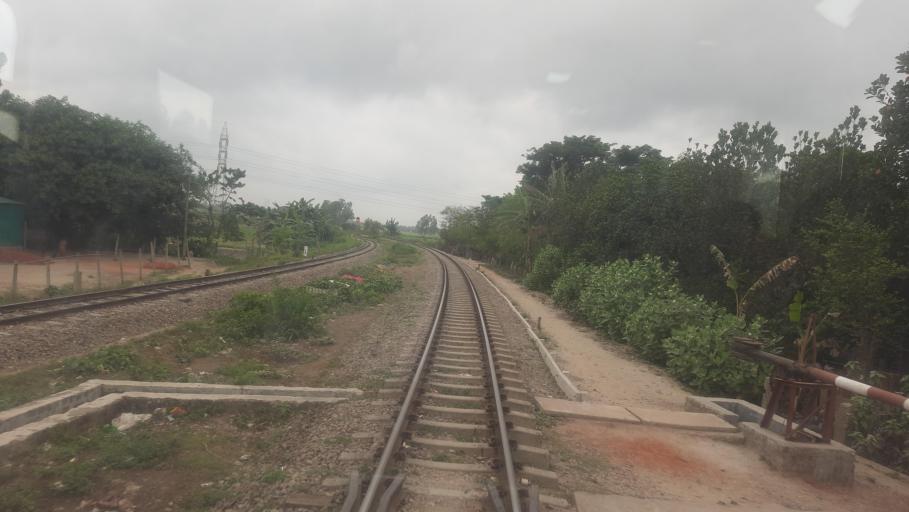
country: BD
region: Dhaka
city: Bhairab Bazar
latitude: 24.0502
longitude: 90.9723
